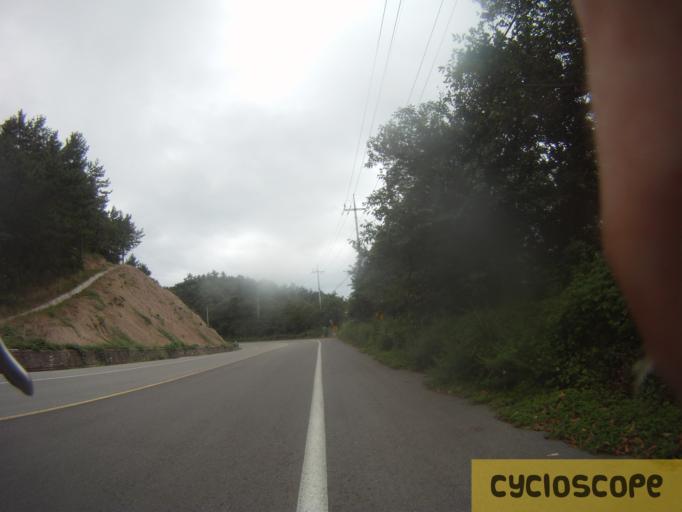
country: KR
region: Jeollanam-do
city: Beolgyo
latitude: 34.8425
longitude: 127.3444
